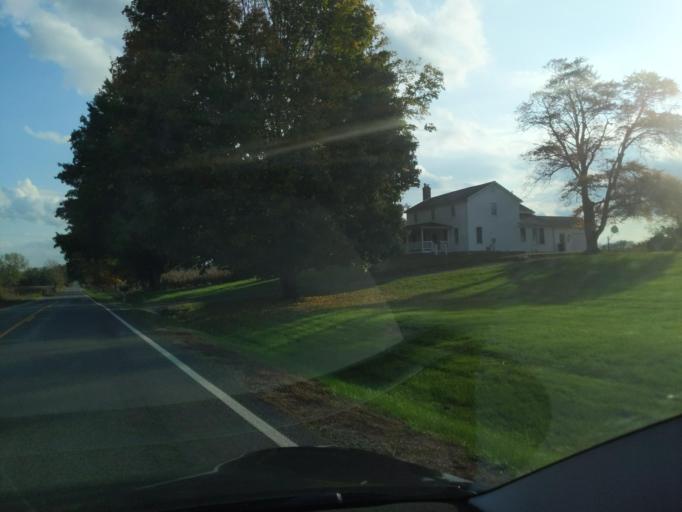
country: US
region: Michigan
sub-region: Ingham County
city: Leslie
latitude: 42.3455
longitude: -84.4629
